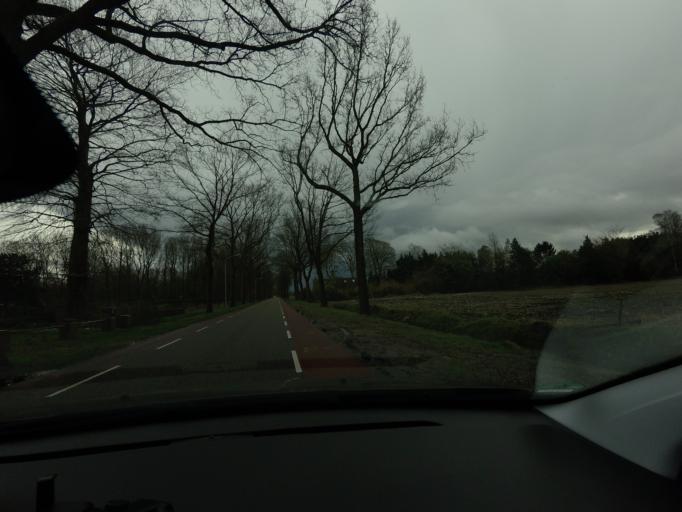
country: NL
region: Drenthe
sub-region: Gemeente Borger-Odoorn
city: Borger
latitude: 52.9821
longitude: 6.7850
